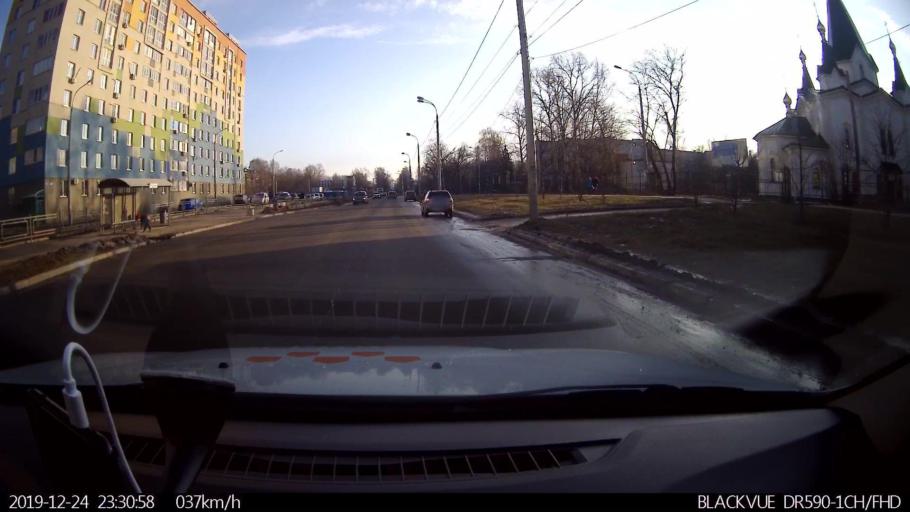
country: RU
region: Nizjnij Novgorod
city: Gorbatovka
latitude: 56.2333
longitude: 43.8447
